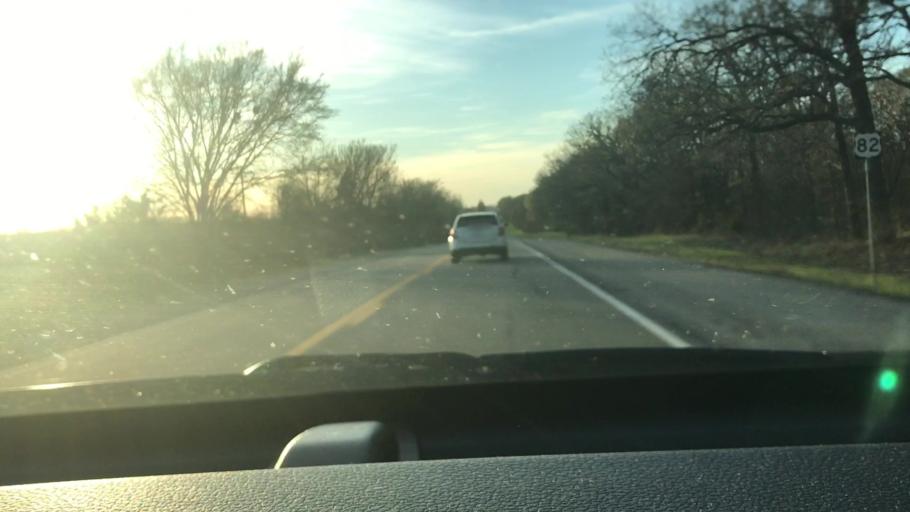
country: US
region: Texas
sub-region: Red River County
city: Clarksville
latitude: 33.5928
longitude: -94.9538
